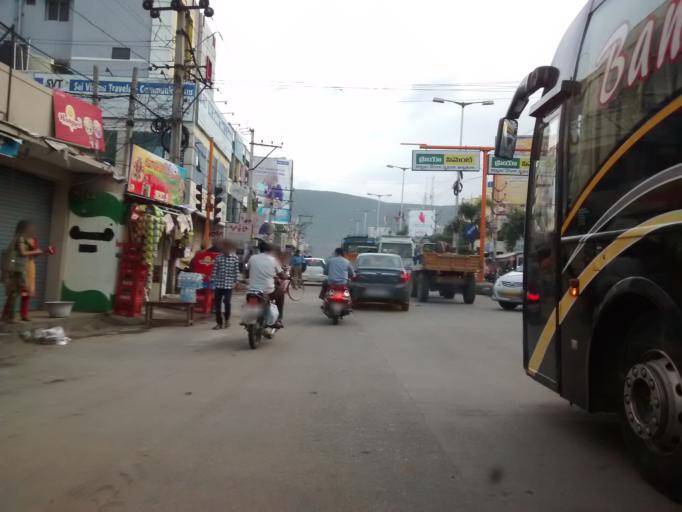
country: IN
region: Andhra Pradesh
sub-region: Chittoor
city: Tirupati
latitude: 13.6368
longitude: 79.4278
